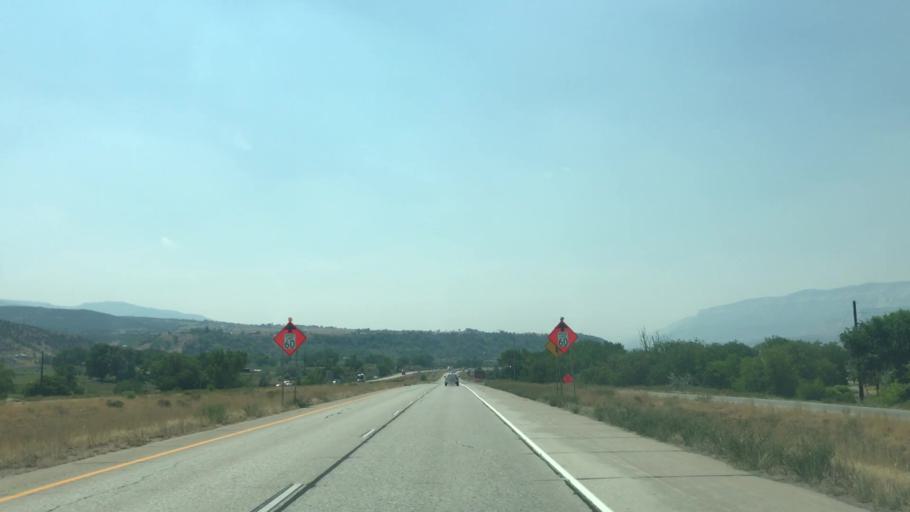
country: US
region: Colorado
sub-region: Garfield County
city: Rifle
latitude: 39.5237
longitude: -107.7793
